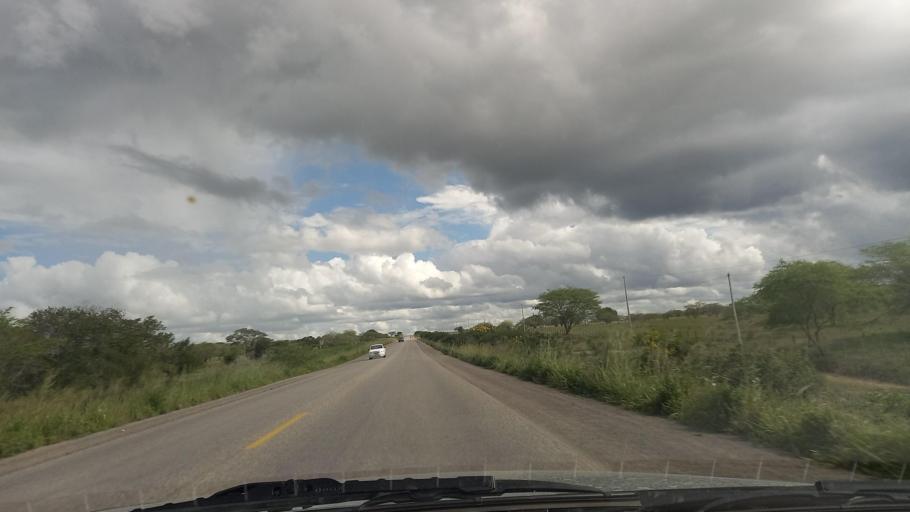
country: BR
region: Pernambuco
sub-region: Cachoeirinha
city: Cachoeirinha
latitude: -8.5145
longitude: -36.2542
